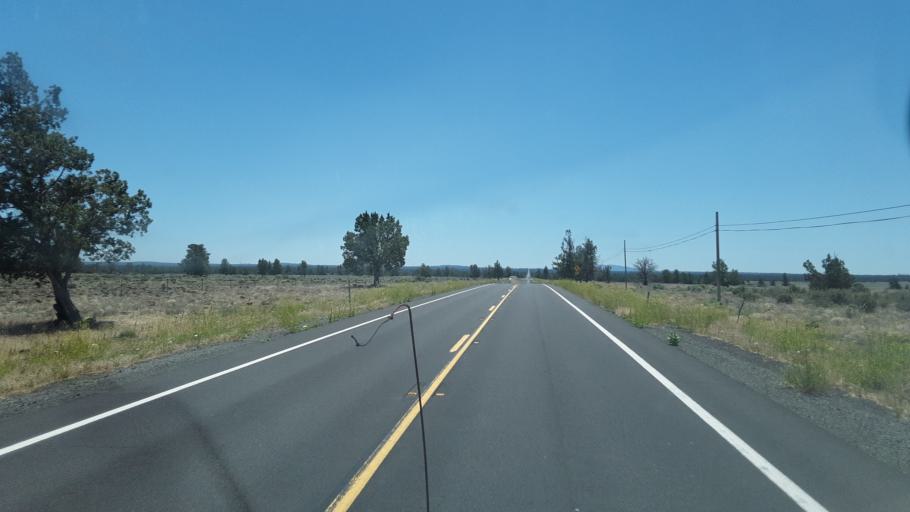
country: US
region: California
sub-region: Siskiyou County
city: Tulelake
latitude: 41.6888
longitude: -121.2709
